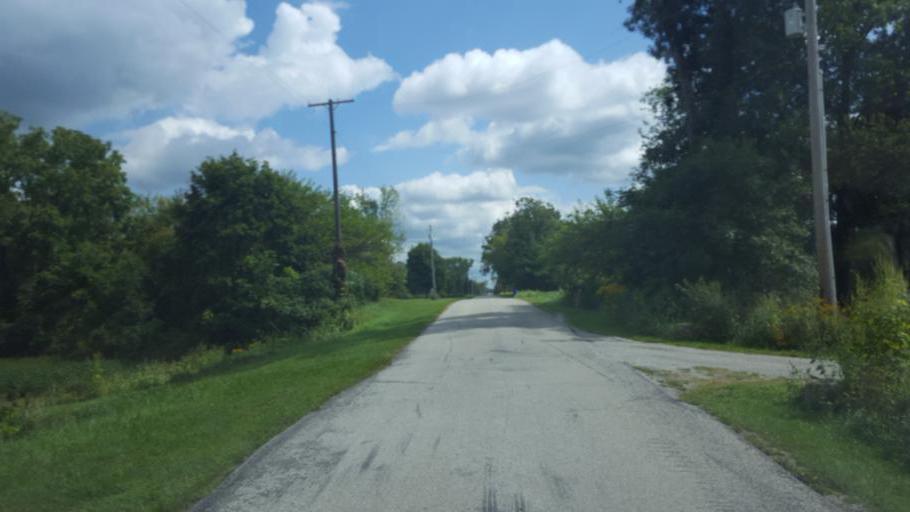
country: US
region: Ohio
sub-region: Huron County
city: Monroeville
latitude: 41.1760
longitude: -82.7311
